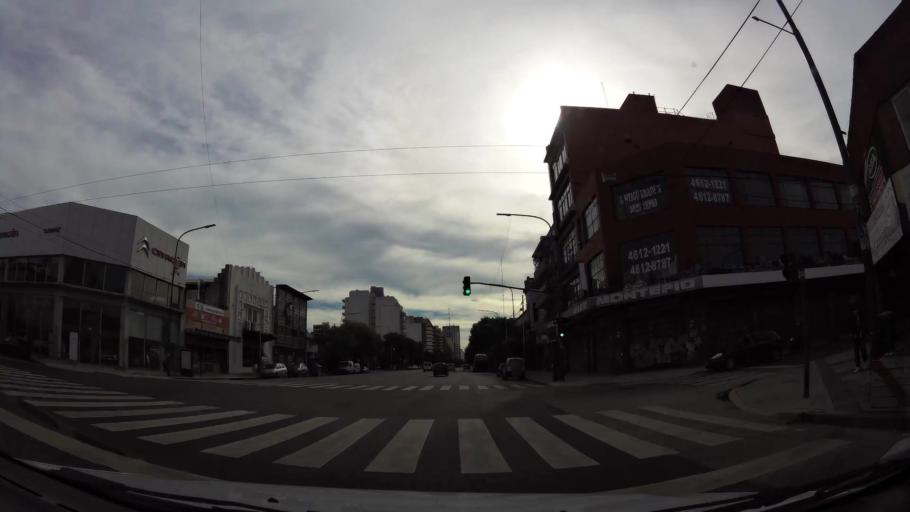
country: AR
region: Buenos Aires F.D.
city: Villa Santa Rita
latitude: -34.6316
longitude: -58.4734
